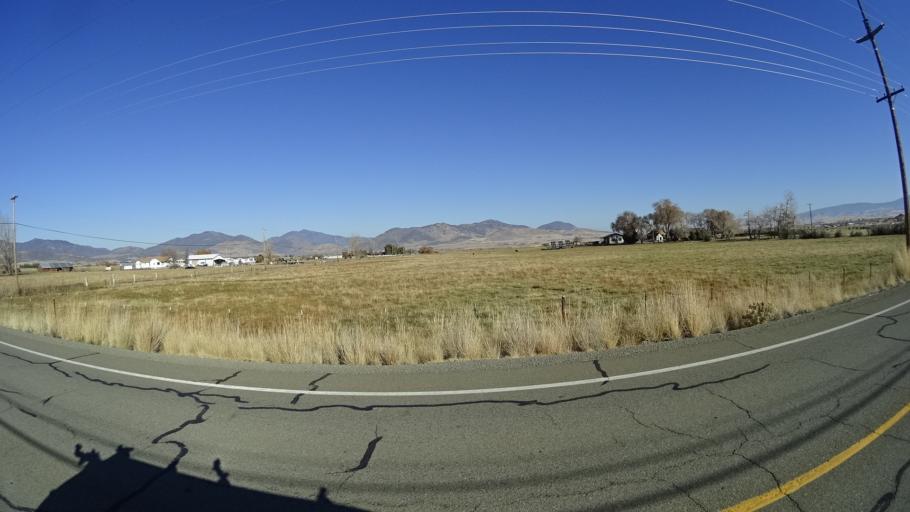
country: US
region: California
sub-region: Siskiyou County
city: Montague
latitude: 41.7056
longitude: -122.5588
